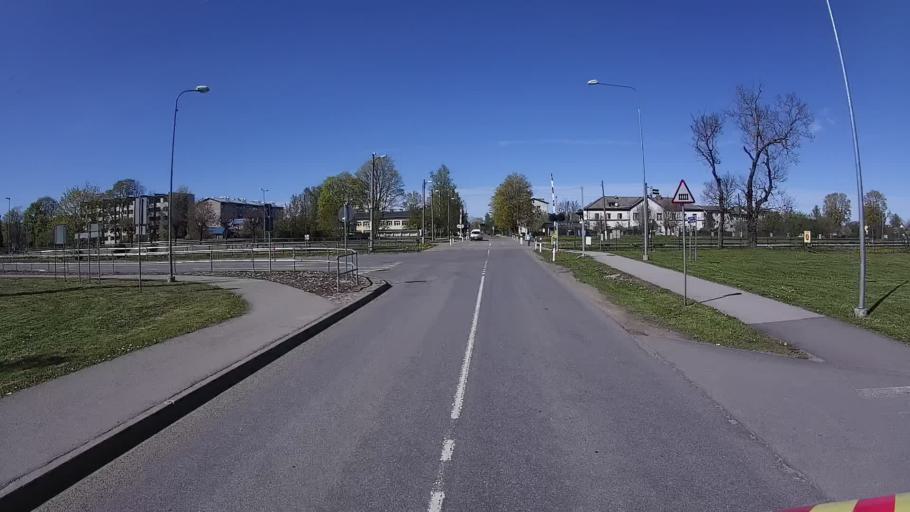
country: EE
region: Laeaene-Virumaa
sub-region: Tapa vald
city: Tapa
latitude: 59.2652
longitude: 25.9657
